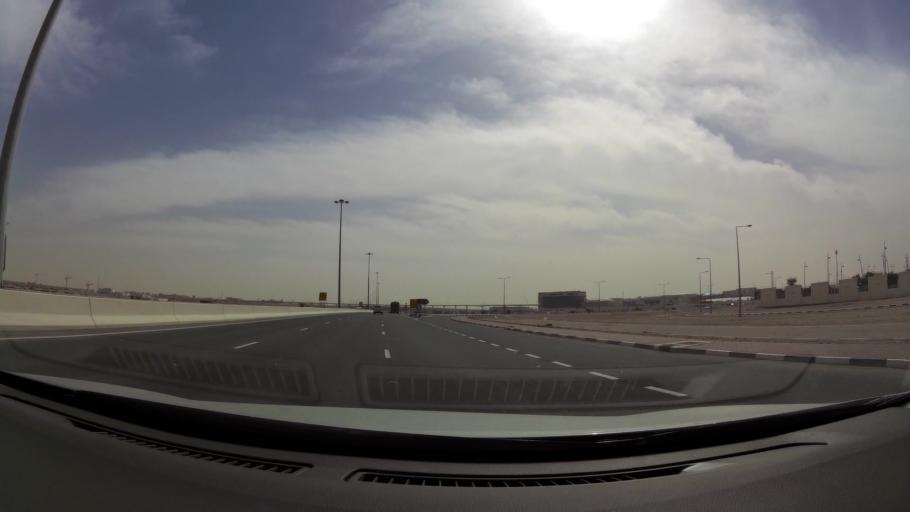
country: QA
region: Baladiyat ar Rayyan
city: Ar Rayyan
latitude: 25.3300
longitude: 51.3593
